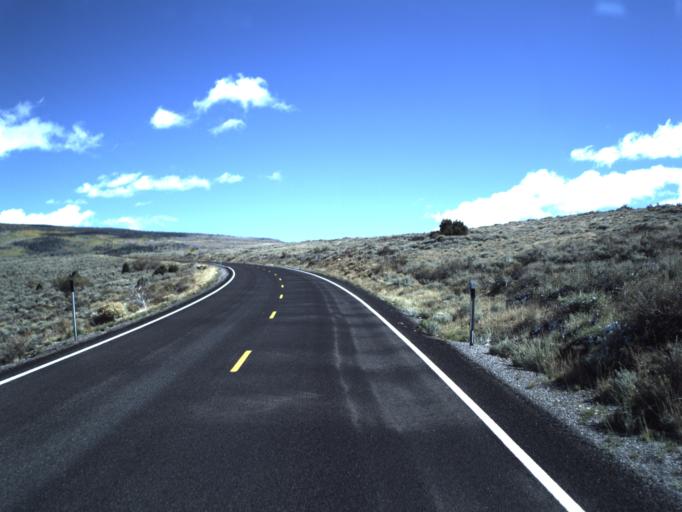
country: US
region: Utah
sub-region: Wayne County
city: Loa
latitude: 38.4937
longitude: -111.8121
